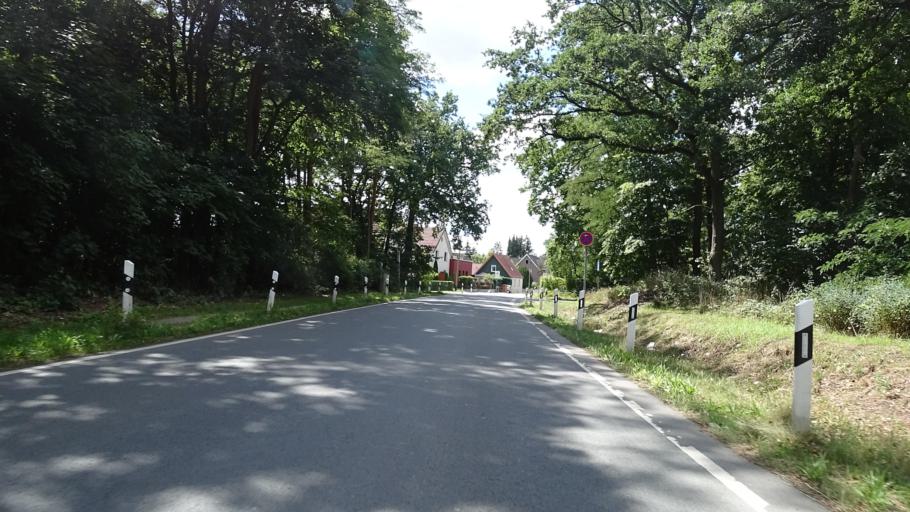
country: DE
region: North Rhine-Westphalia
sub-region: Regierungsbezirk Detmold
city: Steinhagen
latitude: 51.9672
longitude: 8.4392
